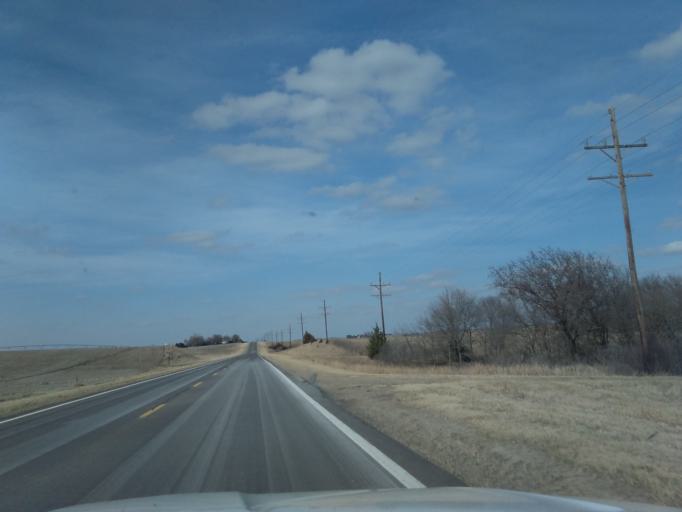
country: US
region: Nebraska
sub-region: Gage County
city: Beatrice
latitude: 40.1413
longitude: -96.9353
